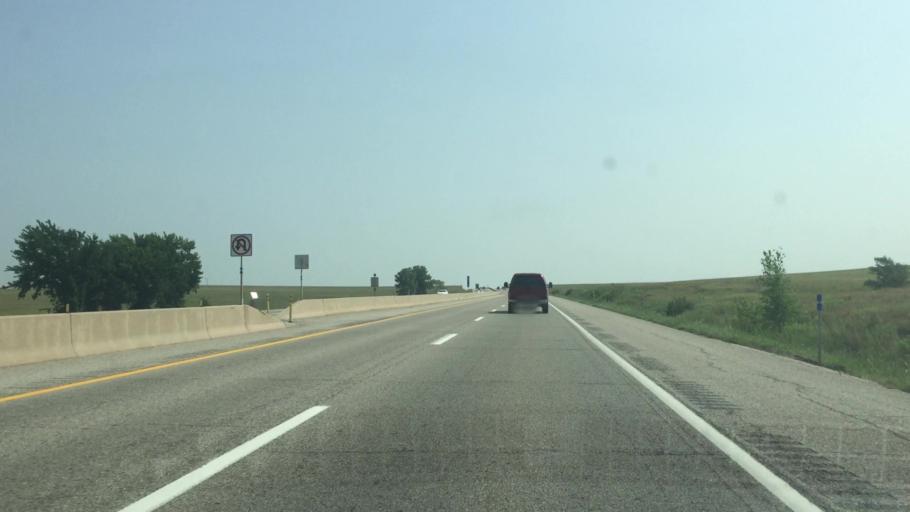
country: US
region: Kansas
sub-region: Lyon County
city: Emporia
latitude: 38.3159
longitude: -96.3305
